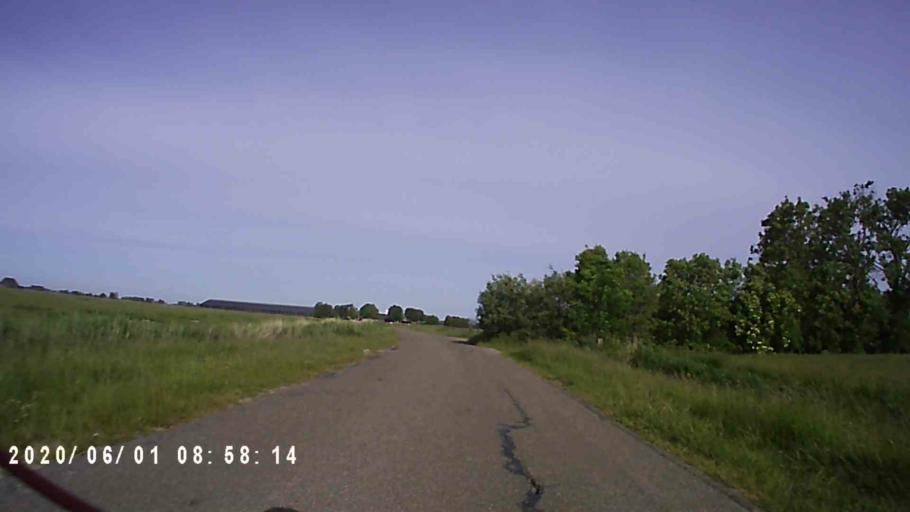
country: NL
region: Friesland
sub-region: Gemeente Ferwerderadiel
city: Hallum
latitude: 53.2814
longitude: 5.8071
